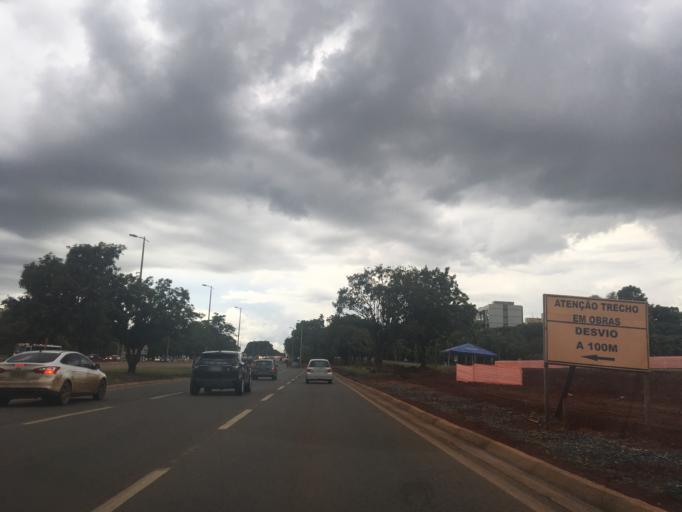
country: BR
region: Federal District
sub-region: Brasilia
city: Brasilia
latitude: -15.7349
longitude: -47.8932
